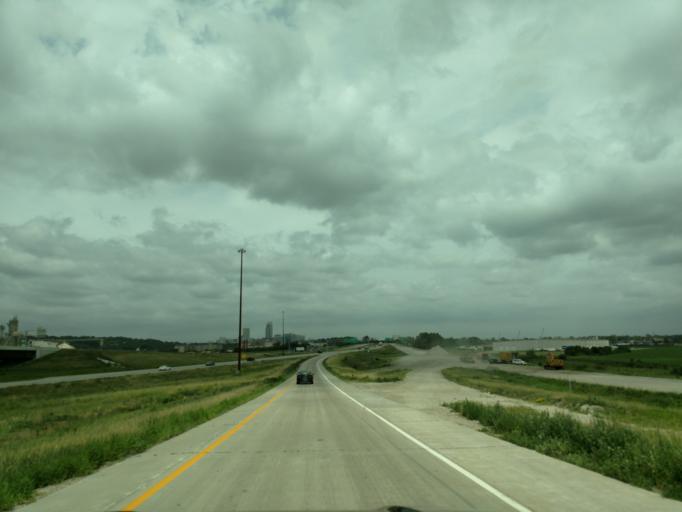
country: US
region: Iowa
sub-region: Pottawattamie County
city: Council Bluffs
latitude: 41.2353
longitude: -95.8970
